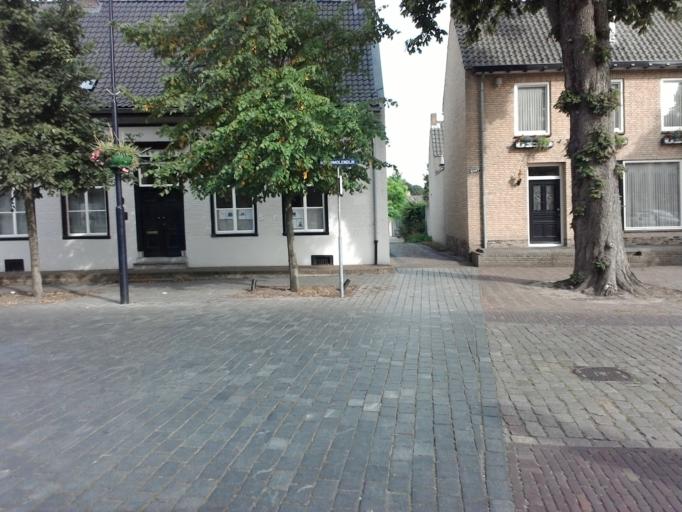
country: NL
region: North Brabant
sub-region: Gemeente Sint-Oedenrode
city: Sint-Oedenrode
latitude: 51.5648
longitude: 5.4614
